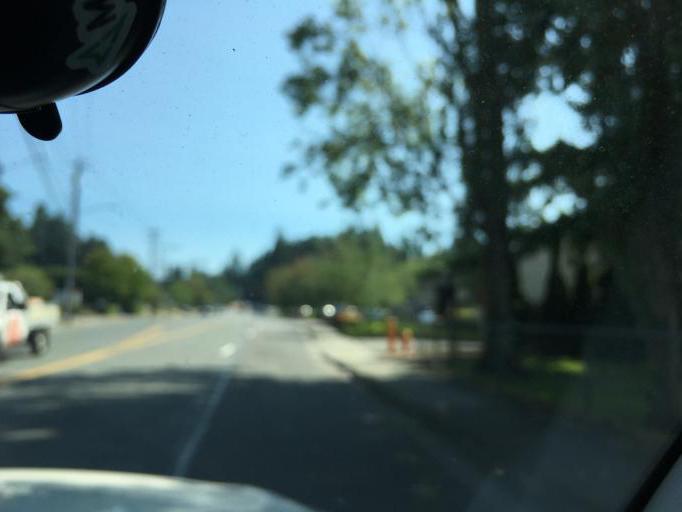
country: US
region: Washington
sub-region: Snohomish County
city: Esperance
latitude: 47.7926
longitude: -122.3669
